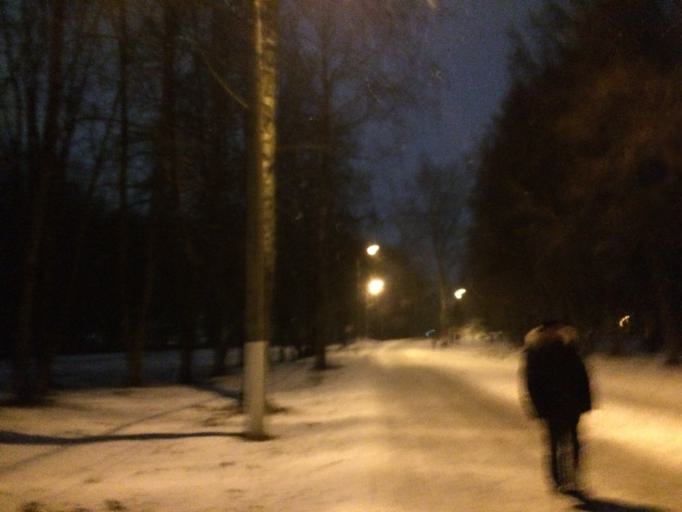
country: RU
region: Tula
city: Tula
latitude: 54.1768
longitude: 37.5899
